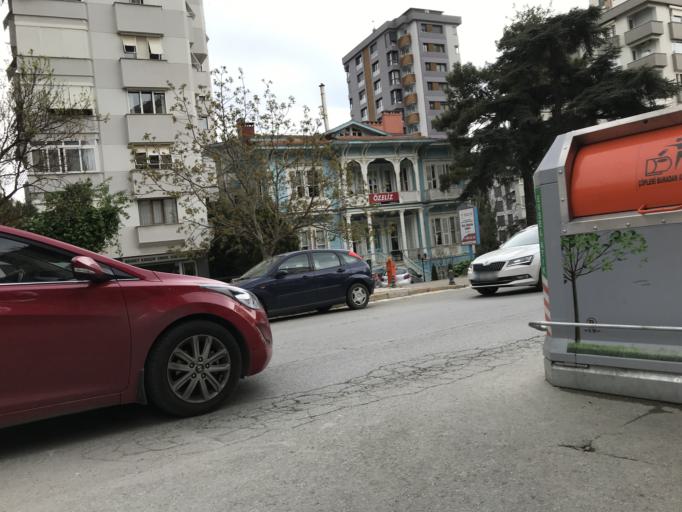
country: TR
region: Istanbul
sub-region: Atasehir
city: Atasehir
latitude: 40.9762
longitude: 29.0644
